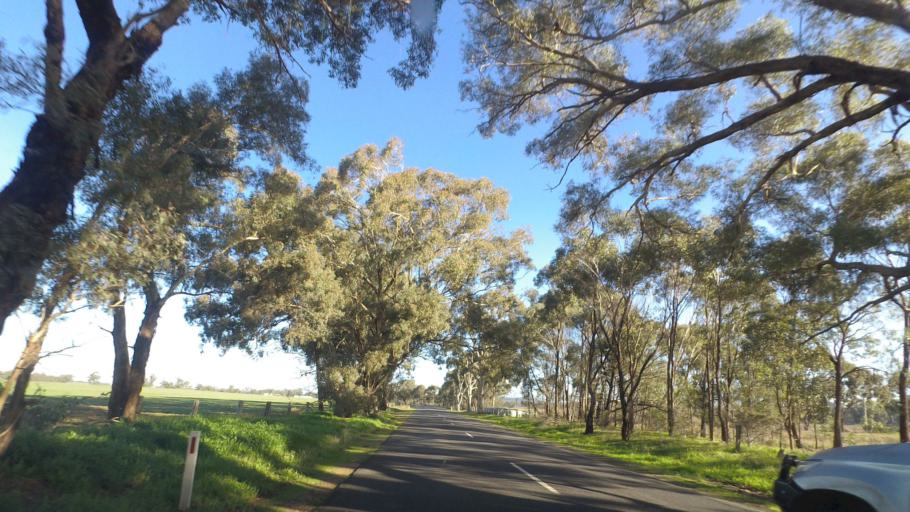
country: AU
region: Victoria
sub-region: Greater Bendigo
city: Epsom
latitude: -36.6838
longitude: 144.5184
